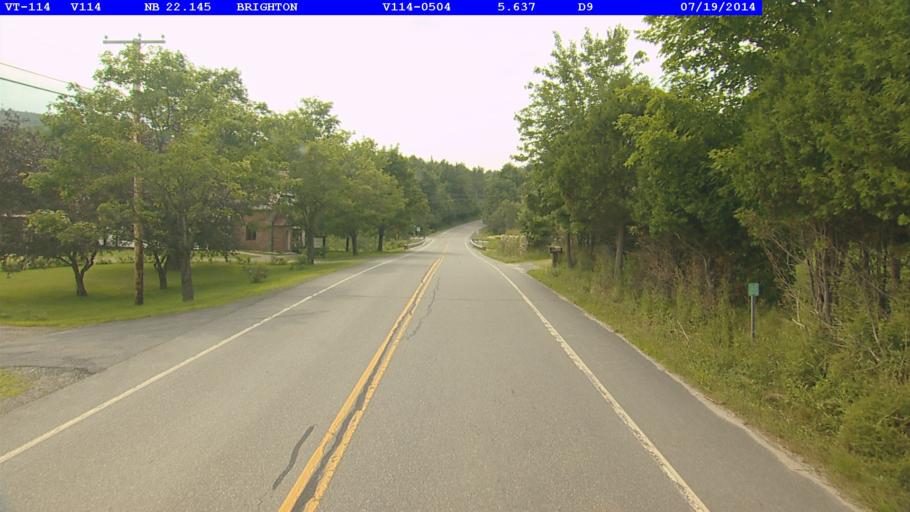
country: US
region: Vermont
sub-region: Caledonia County
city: Lyndonville
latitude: 44.8251
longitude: -71.8995
